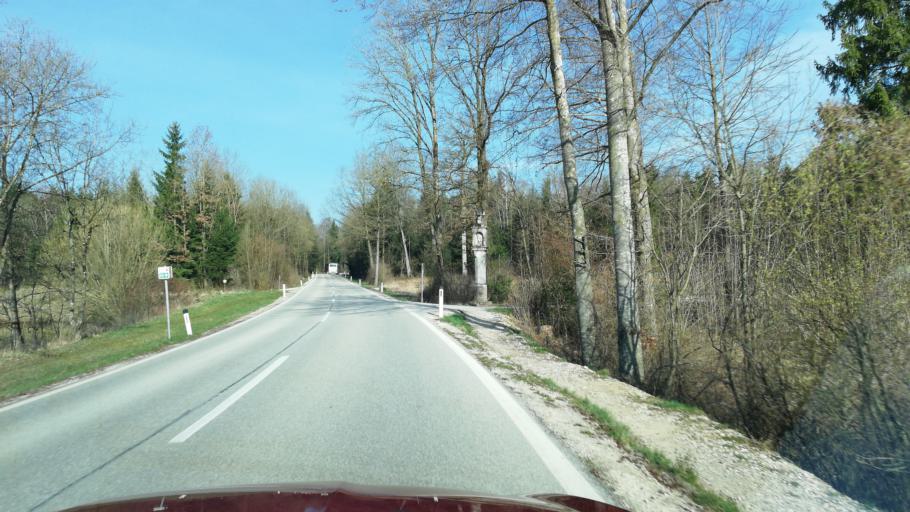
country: AT
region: Upper Austria
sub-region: Politischer Bezirk Kirchdorf an der Krems
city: Kremsmunster
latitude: 48.0807
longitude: 14.1172
